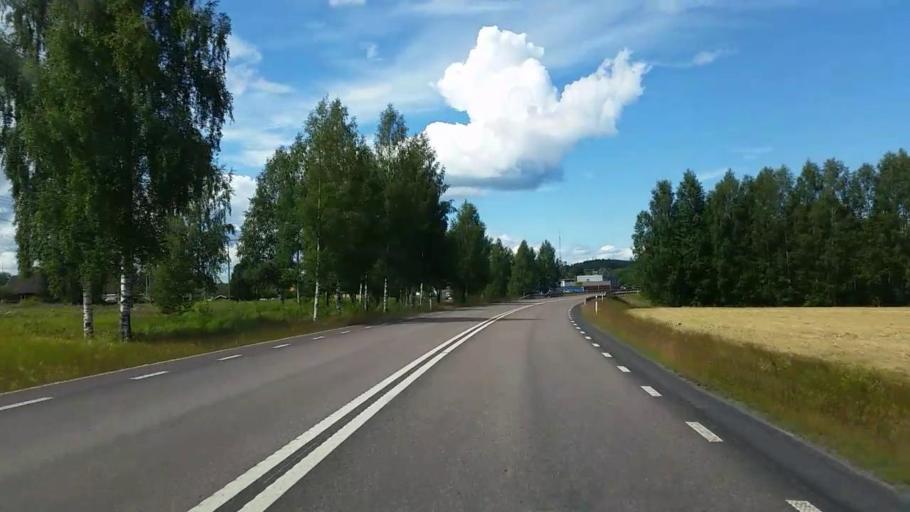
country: SE
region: Dalarna
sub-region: Leksand Municipality
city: Leksand
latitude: 60.7247
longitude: 15.0120
